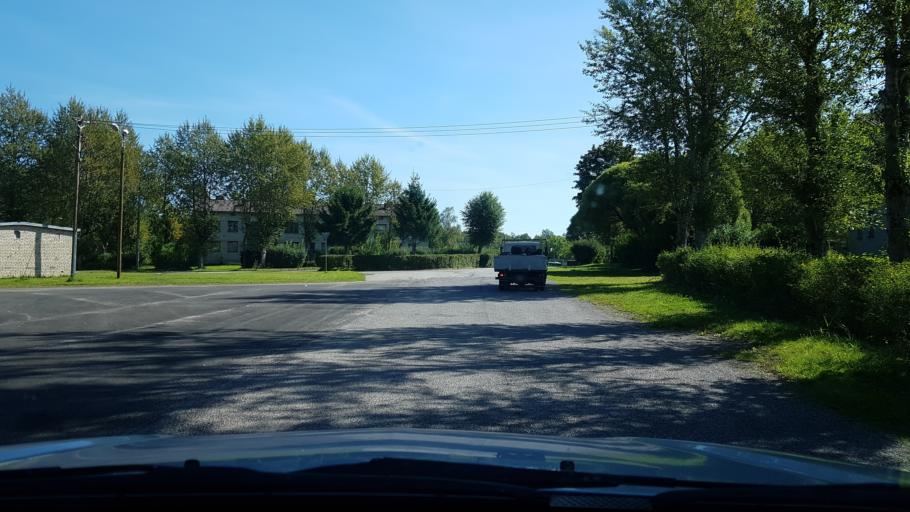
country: EE
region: Ida-Virumaa
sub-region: Sillamaee linn
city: Sillamae
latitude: 59.3204
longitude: 27.7796
